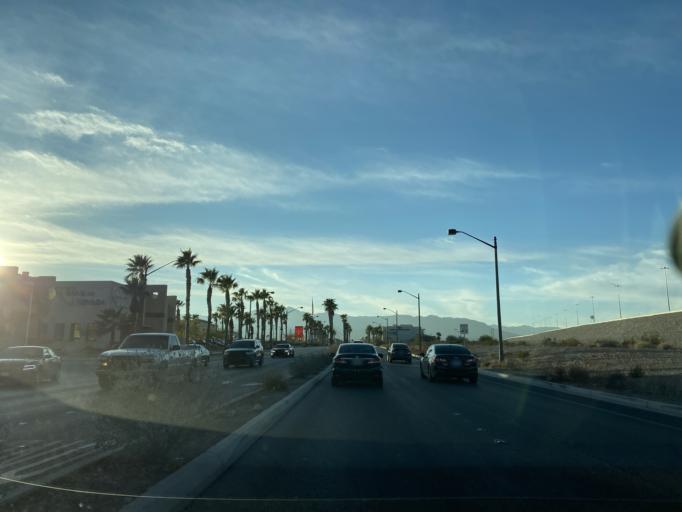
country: US
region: Nevada
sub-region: Clark County
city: Summerlin South
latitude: 36.2774
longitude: -115.2792
